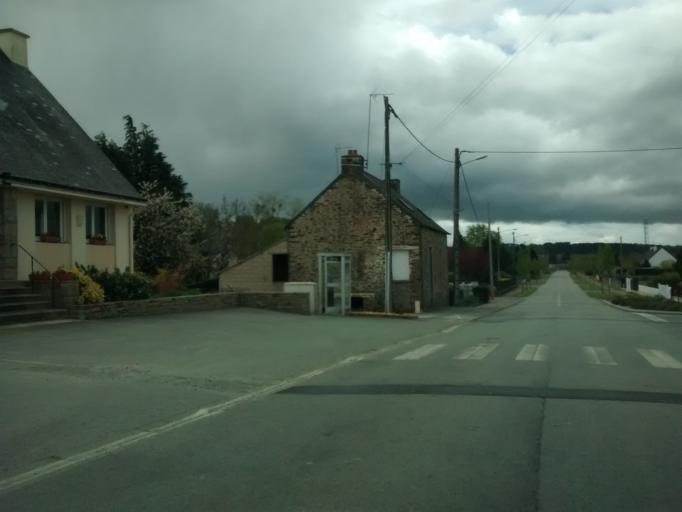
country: FR
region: Brittany
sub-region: Departement du Morbihan
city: Pleucadeuc
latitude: 47.7692
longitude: -2.3176
